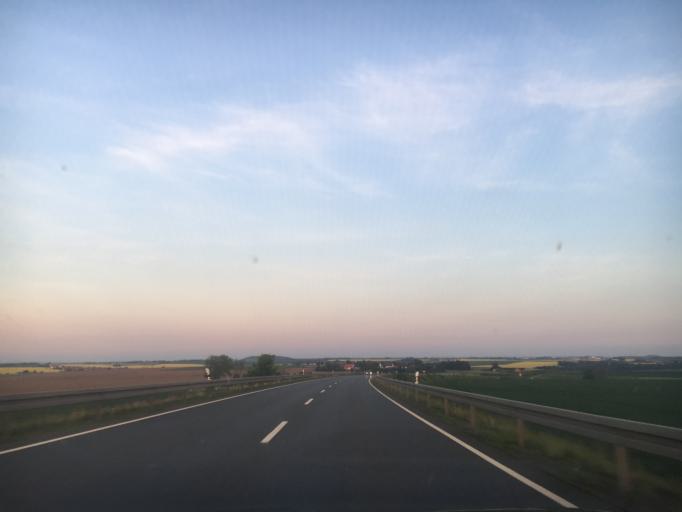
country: DE
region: Thuringia
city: Schwaara
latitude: 50.9335
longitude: 12.1282
